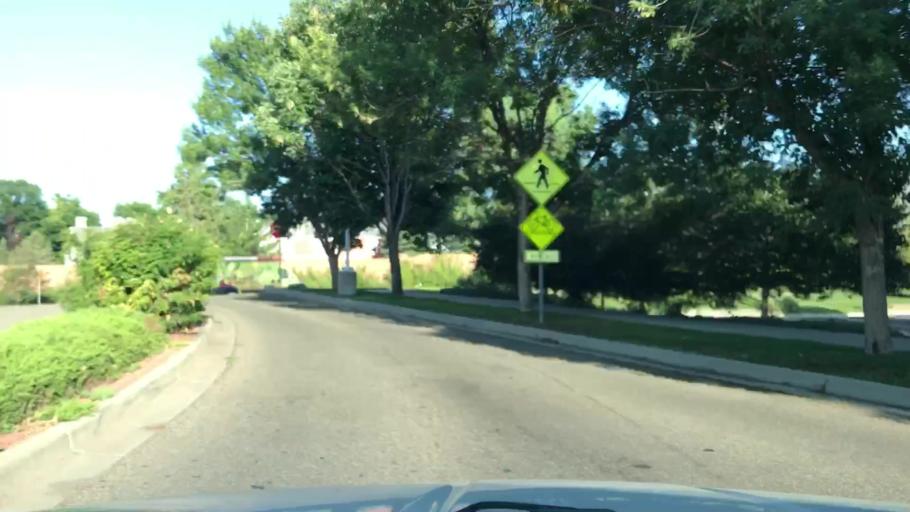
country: US
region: Colorado
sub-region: Boulder County
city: Lafayette
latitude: 39.9889
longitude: -105.0976
